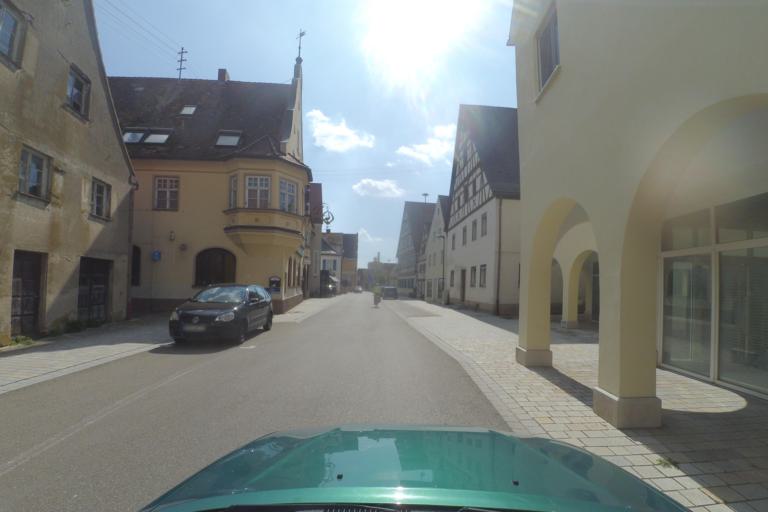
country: DE
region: Bavaria
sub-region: Swabia
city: Oettingen in Bayern
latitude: 48.9512
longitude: 10.6034
